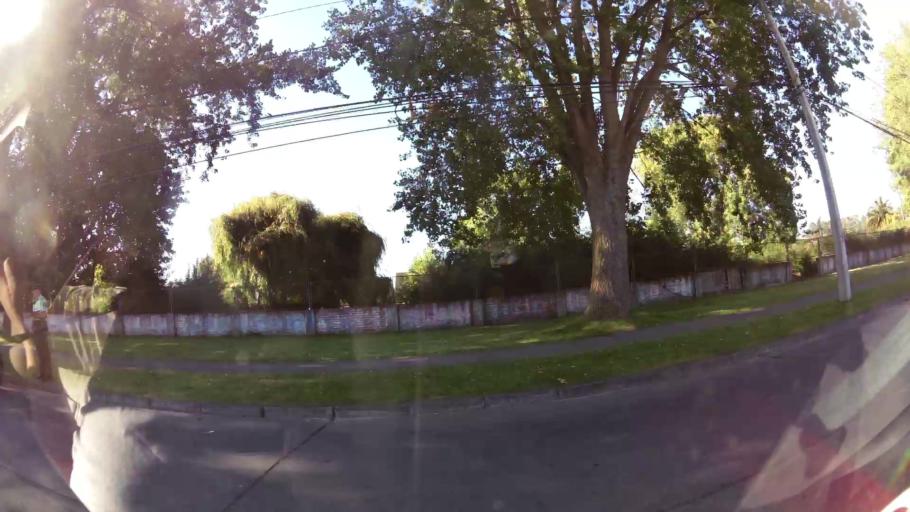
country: CL
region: Biobio
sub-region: Provincia de Concepcion
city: Concepcion
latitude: -36.8440
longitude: -73.0996
